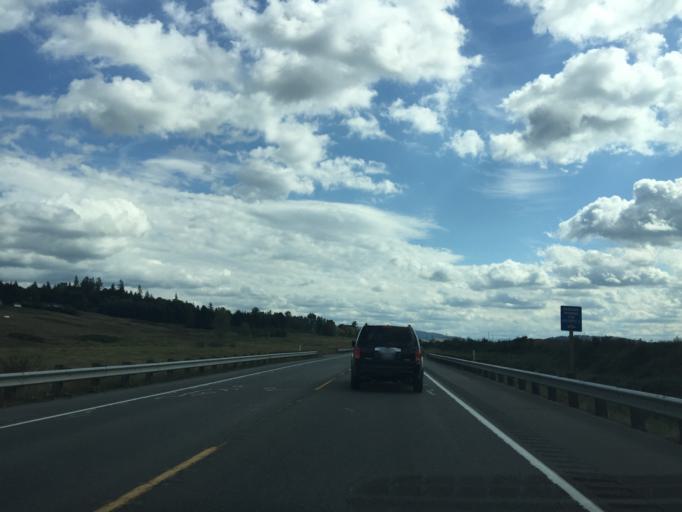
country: US
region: Washington
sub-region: Snohomish County
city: Monroe
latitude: 47.8814
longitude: -122.0205
